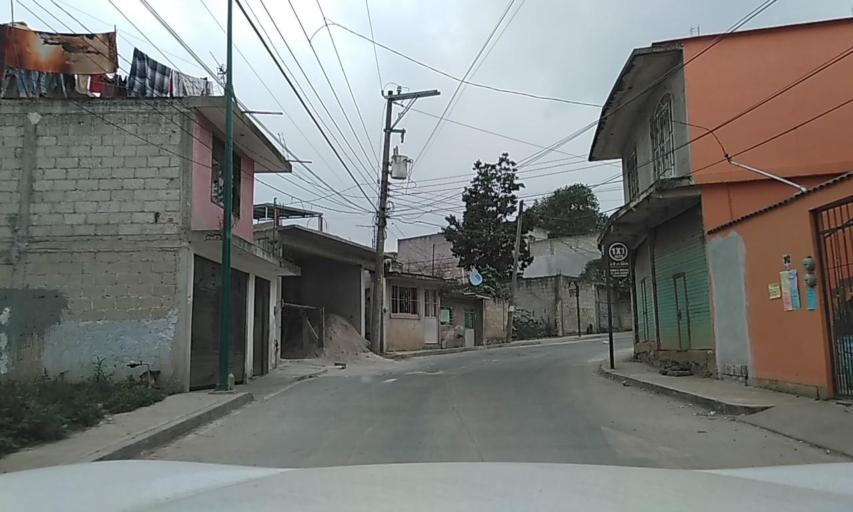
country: MX
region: Veracruz
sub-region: Jilotepec
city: El Pueblito (Garbanzal)
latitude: 19.5708
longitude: -96.8952
